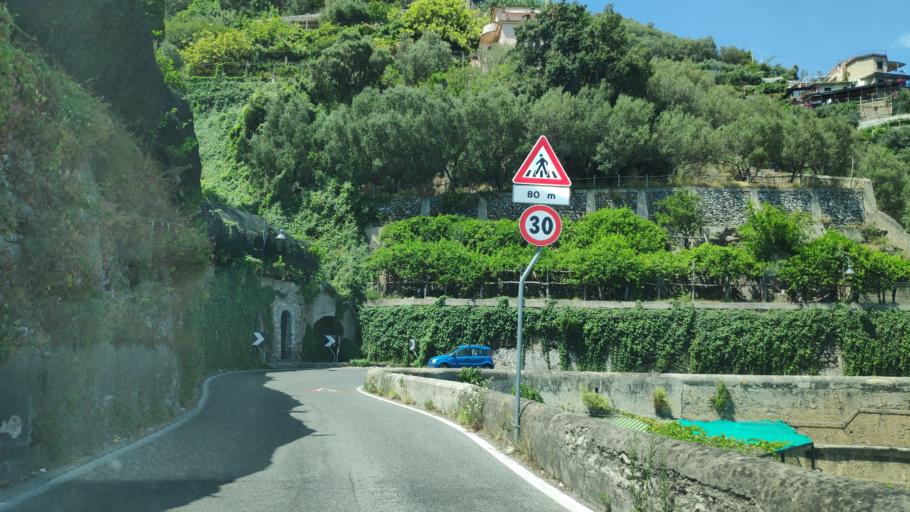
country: IT
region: Campania
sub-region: Provincia di Salerno
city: Ravello
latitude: 40.6433
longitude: 14.6178
